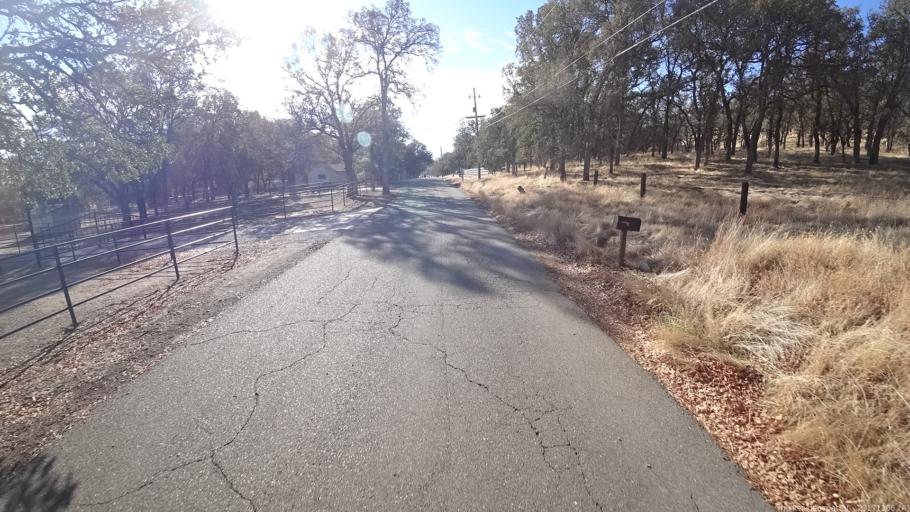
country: US
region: California
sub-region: Shasta County
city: Palo Cedro
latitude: 40.5357
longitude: -122.2477
